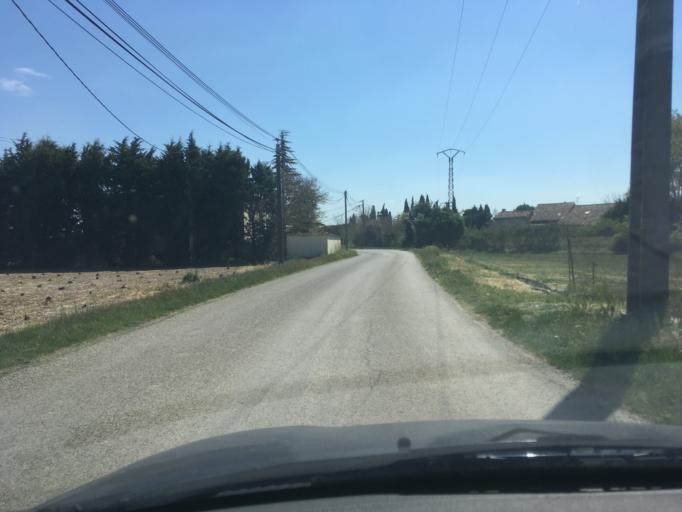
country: FR
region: Provence-Alpes-Cote d'Azur
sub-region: Departement du Vaucluse
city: Sarrians
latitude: 44.0992
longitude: 4.9444
